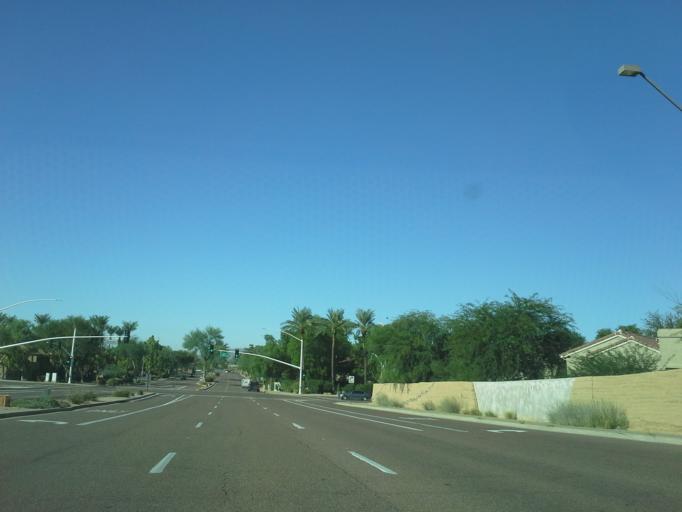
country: US
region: Arizona
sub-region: Maricopa County
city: Paradise Valley
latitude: 33.6247
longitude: -111.8710
